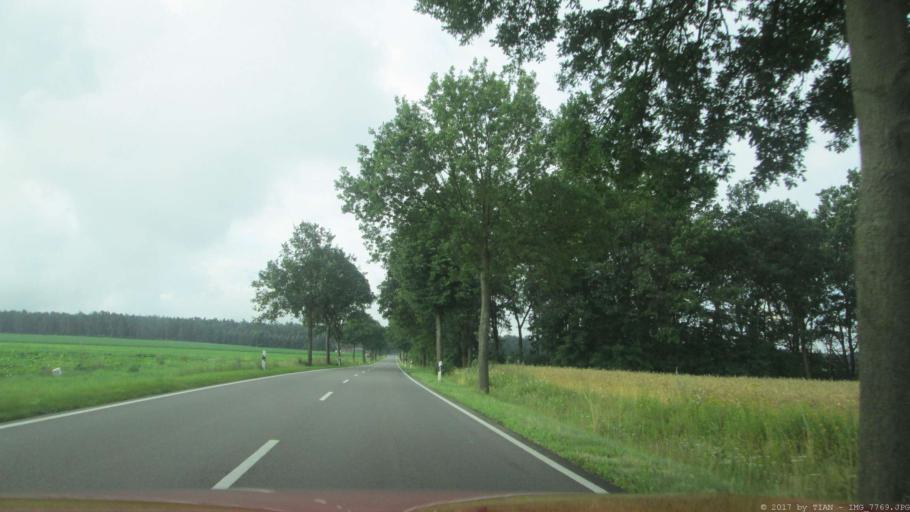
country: DE
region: Lower Saxony
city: Bodenteich
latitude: 52.7938
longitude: 10.7152
